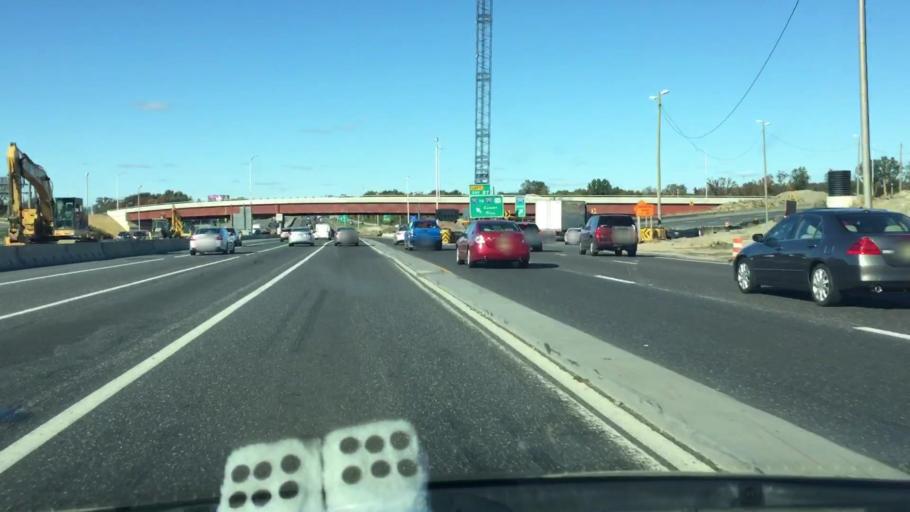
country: US
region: New Jersey
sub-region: Camden County
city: Bellmawr
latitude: 39.8725
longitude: -75.1018
